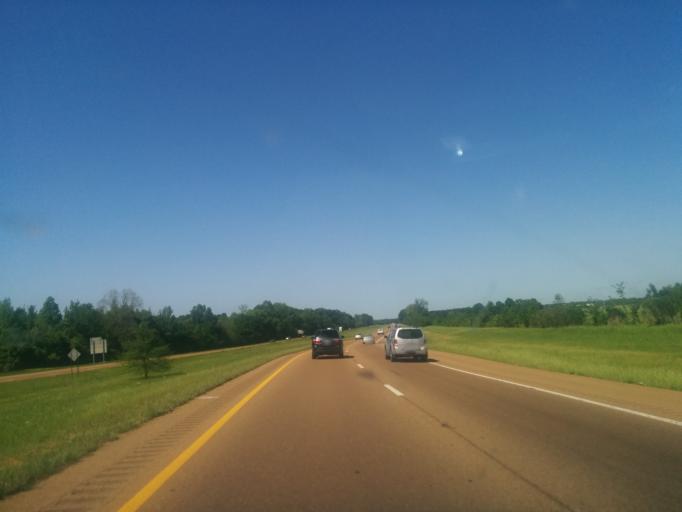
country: US
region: Mississippi
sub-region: Madison County
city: Madison
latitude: 32.4866
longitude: -90.1299
